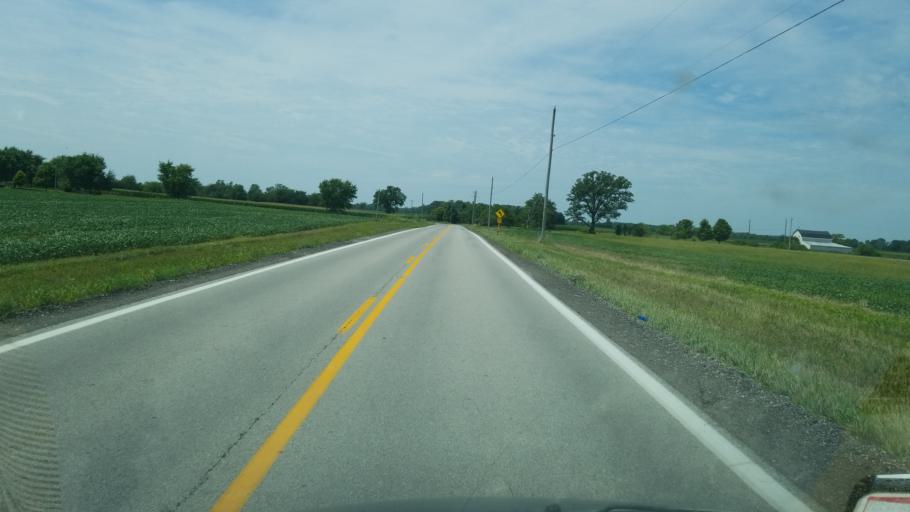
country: US
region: Ohio
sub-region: Madison County
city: West Jefferson
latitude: 39.8791
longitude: -83.3255
